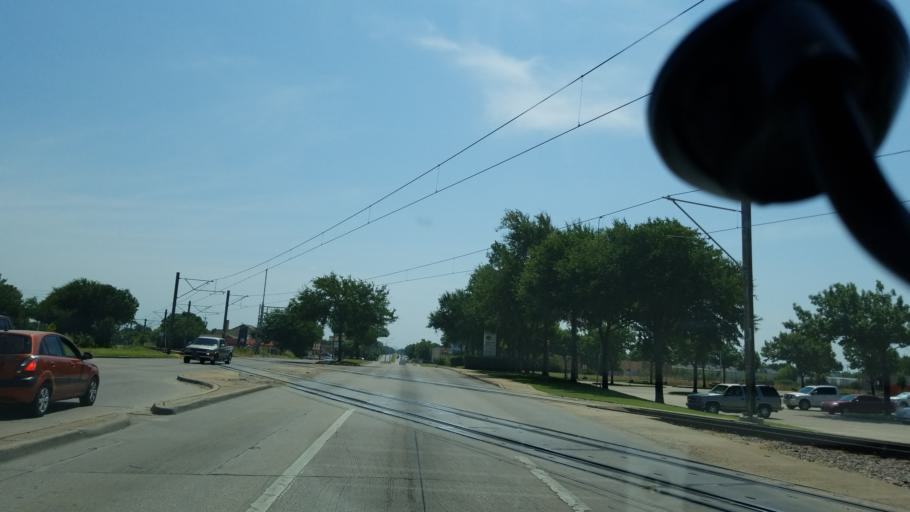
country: US
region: Texas
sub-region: Dallas County
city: Cockrell Hill
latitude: 32.7203
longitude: -96.8705
